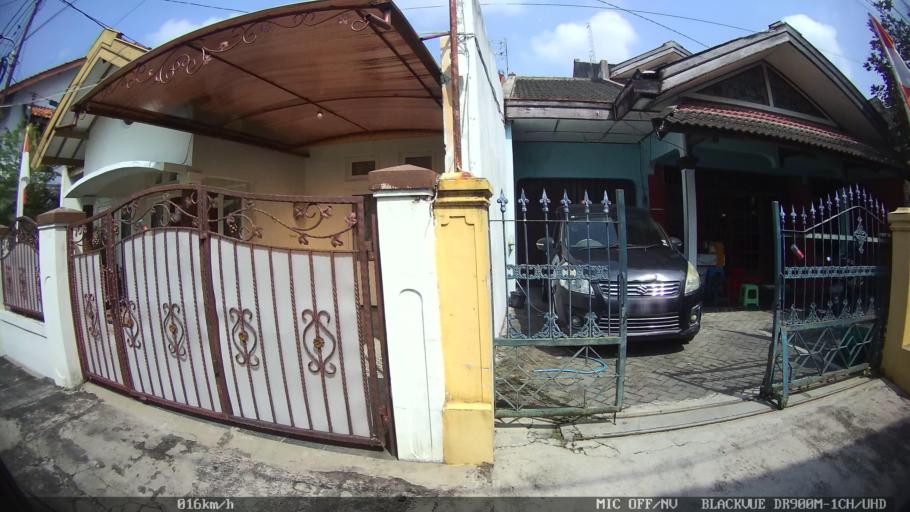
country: ID
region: Daerah Istimewa Yogyakarta
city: Yogyakarta
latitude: -7.8086
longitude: 110.3800
